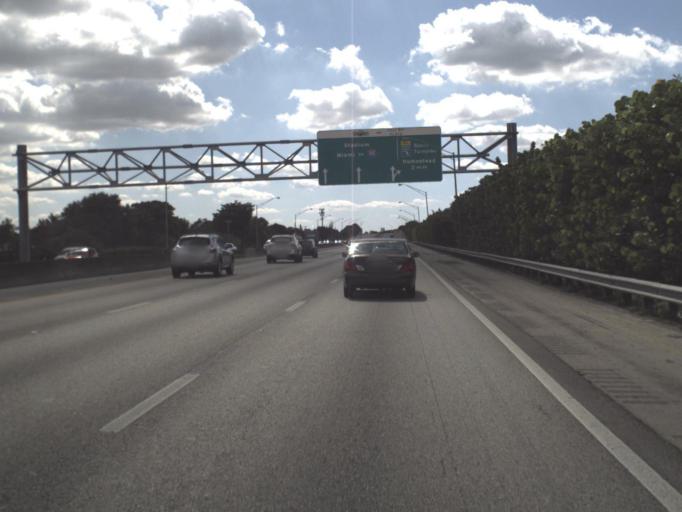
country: US
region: Florida
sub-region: Broward County
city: Pembroke Pines
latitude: 26.0011
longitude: -80.2186
